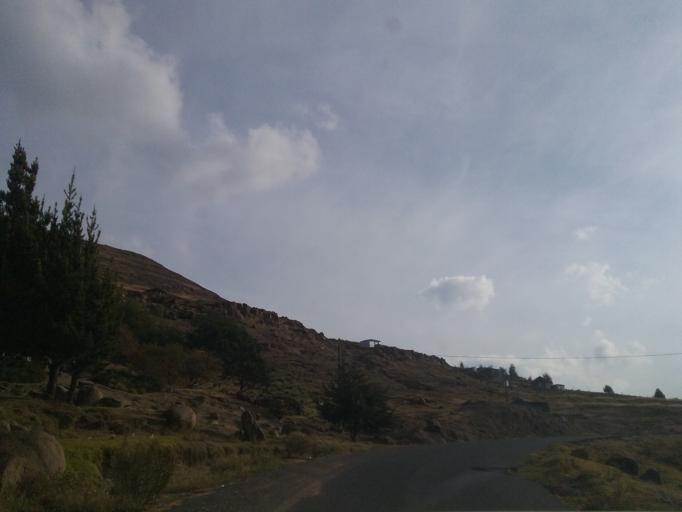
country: LS
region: Quthing
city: Quthing
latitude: -30.1947
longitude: 28.1165
